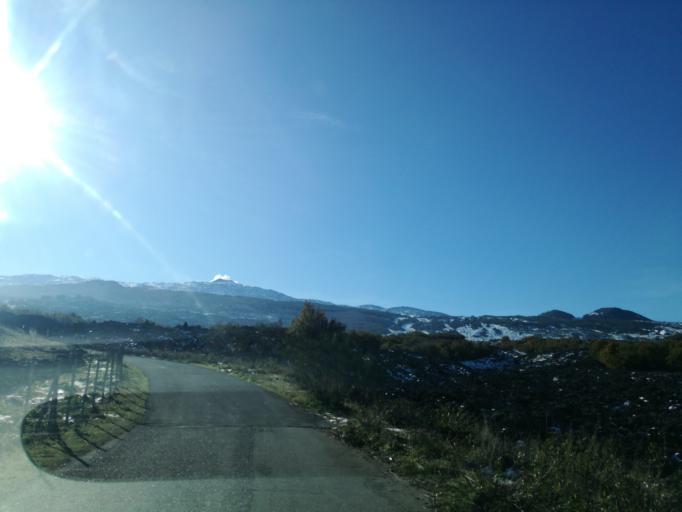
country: IT
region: Sicily
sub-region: Catania
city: Randazzo
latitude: 37.8619
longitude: 14.9795
